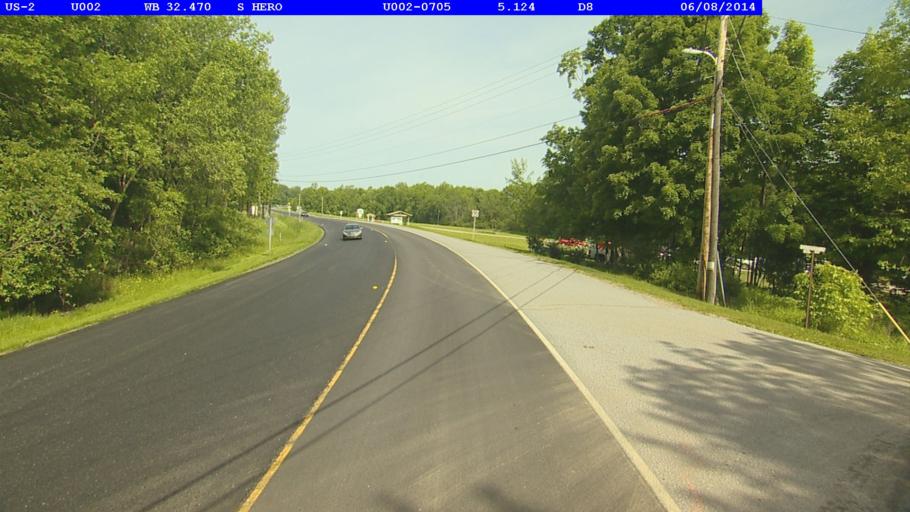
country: US
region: Vermont
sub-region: Chittenden County
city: Colchester
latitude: 44.6365
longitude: -73.2674
